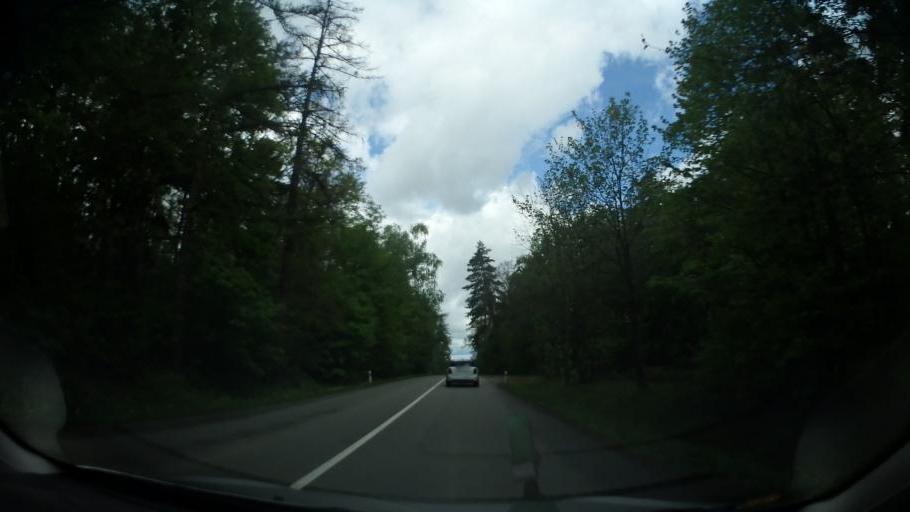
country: CZ
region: South Moravian
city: Ricany
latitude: 49.2256
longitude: 16.3635
